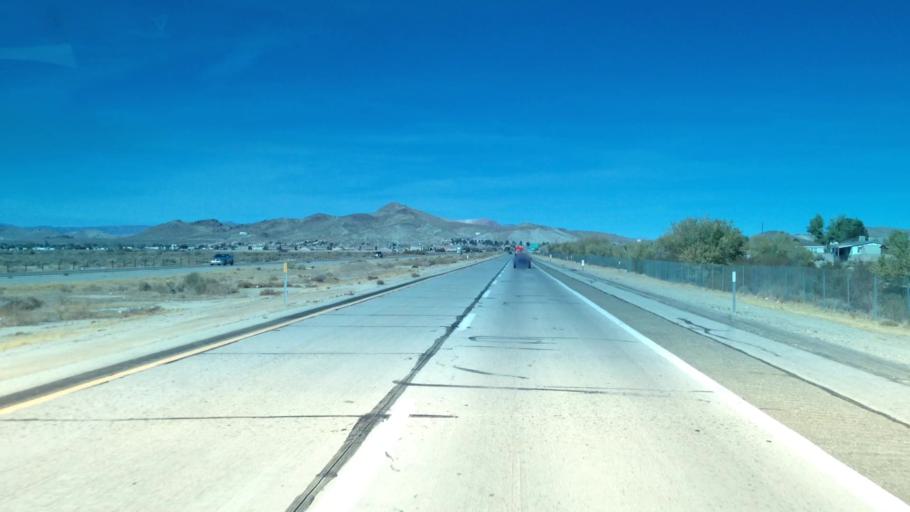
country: US
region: California
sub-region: Kern County
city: Rosamond
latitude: 34.8426
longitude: -118.1708
